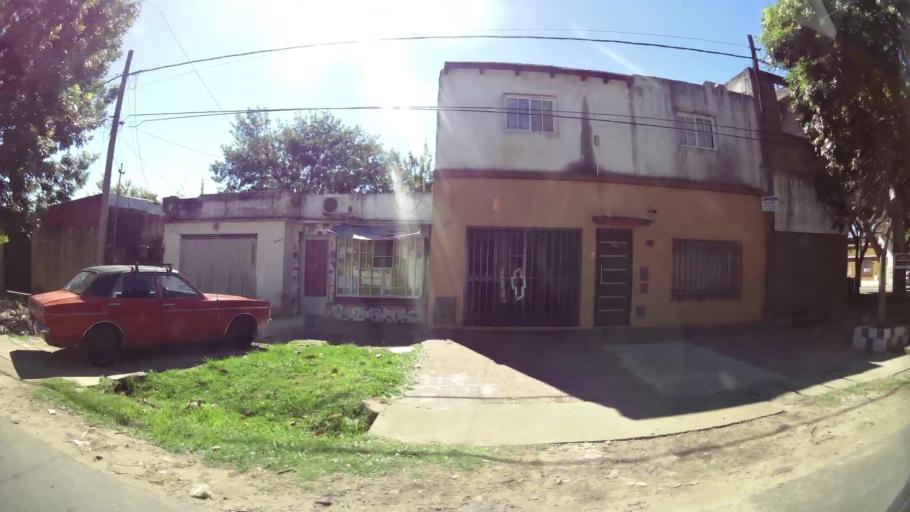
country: AR
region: Santa Fe
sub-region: Departamento de Rosario
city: Rosario
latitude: -32.9557
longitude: -60.6890
